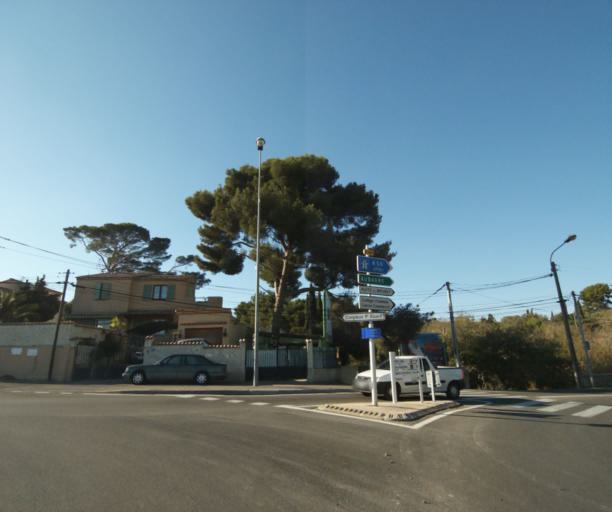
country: FR
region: Provence-Alpes-Cote d'Azur
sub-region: Departement des Bouches-du-Rhone
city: La Ciotat
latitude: 43.1843
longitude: 5.5994
